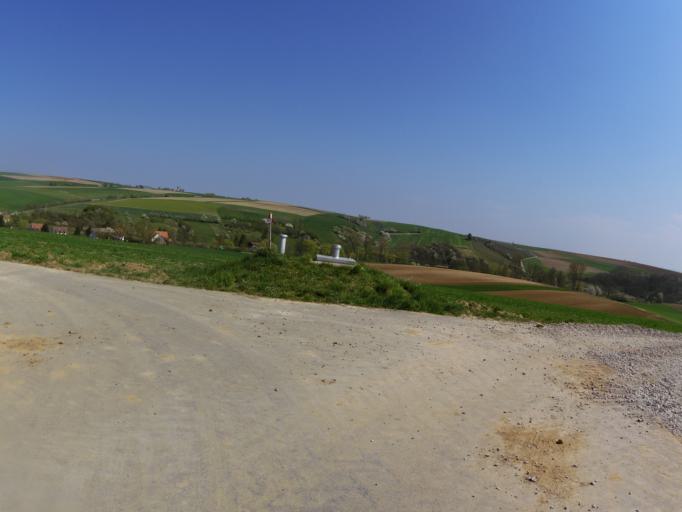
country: DE
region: Bavaria
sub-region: Regierungsbezirk Unterfranken
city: Dettelbach
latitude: 49.8163
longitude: 10.1489
